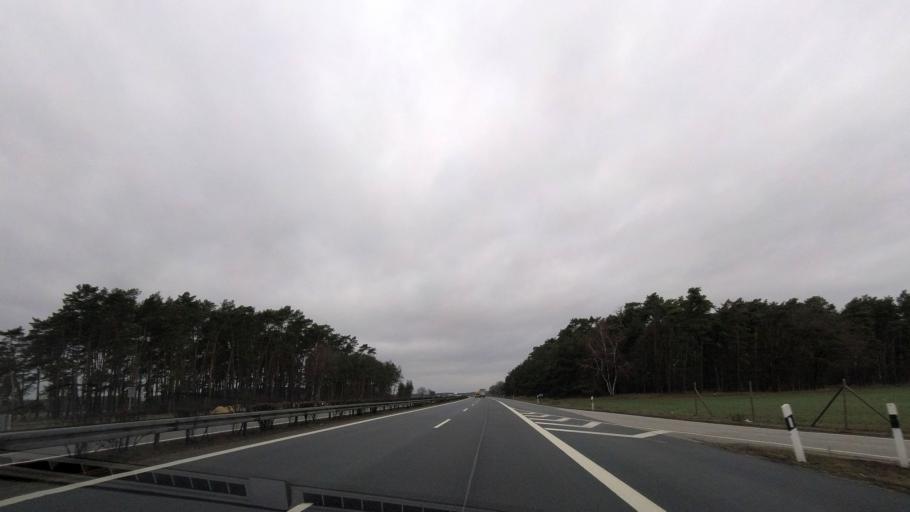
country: DE
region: Mecklenburg-Vorpommern
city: Sulstorf
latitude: 53.4636
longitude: 11.3406
